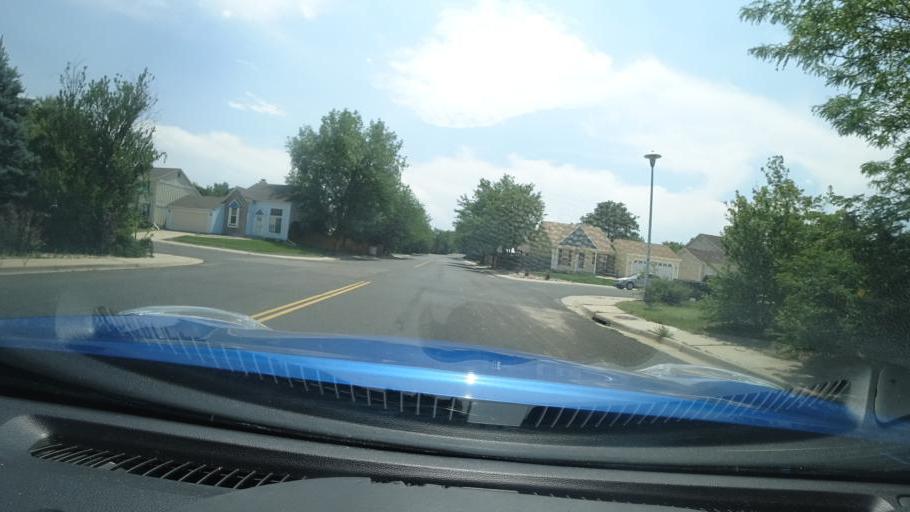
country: US
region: Colorado
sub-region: Adams County
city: Aurora
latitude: 39.6674
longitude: -104.7591
